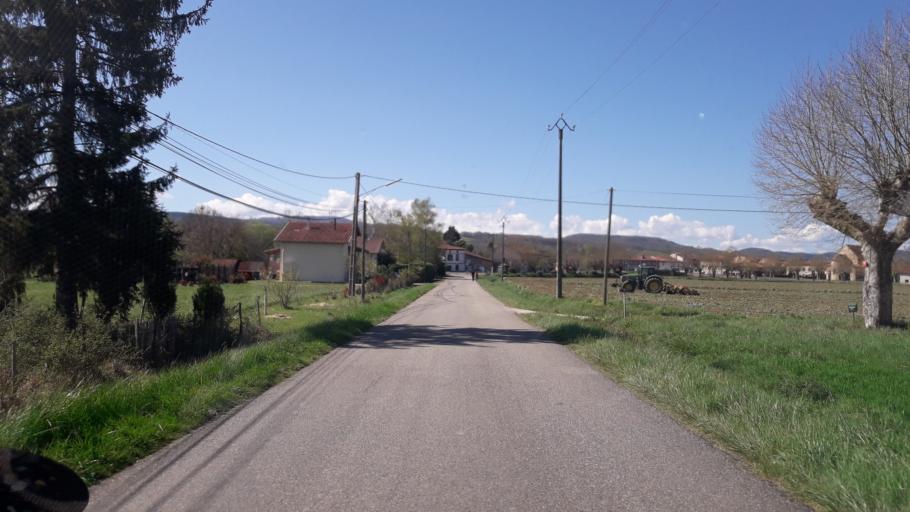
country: FR
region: Midi-Pyrenees
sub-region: Departement de la Haute-Garonne
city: Montesquieu-Volvestre
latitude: 43.1464
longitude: 1.3123
